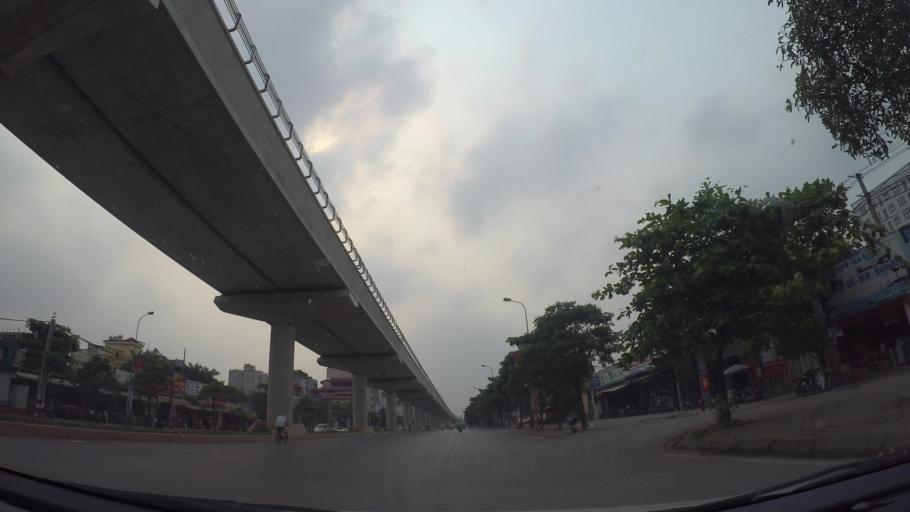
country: VN
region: Ha Noi
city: Cau Dien
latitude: 21.0445
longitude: 105.7541
